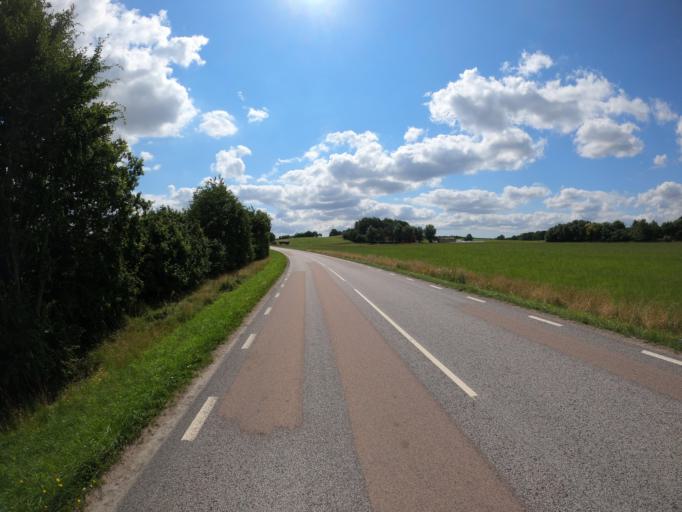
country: SE
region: Skane
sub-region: Lunds Kommun
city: Veberod
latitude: 55.6075
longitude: 13.4876
